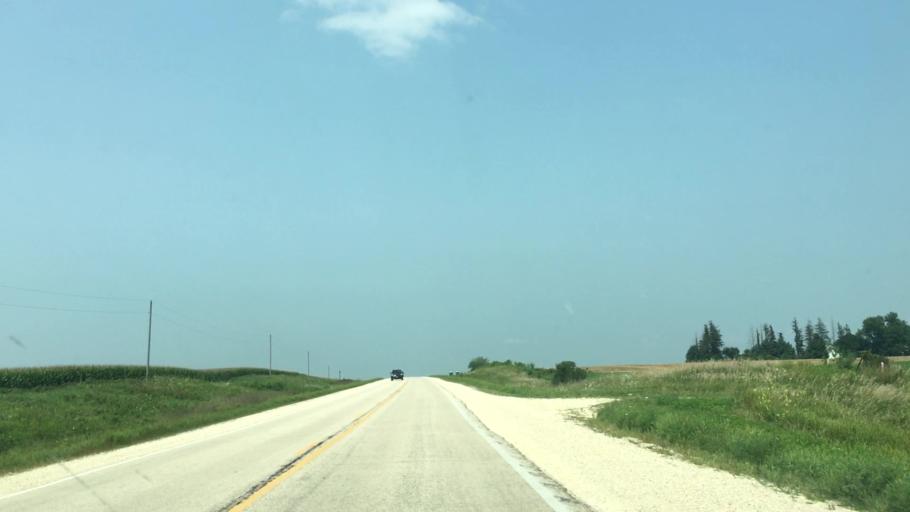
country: US
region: Iowa
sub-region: Fayette County
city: West Union
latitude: 42.9935
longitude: -91.8239
